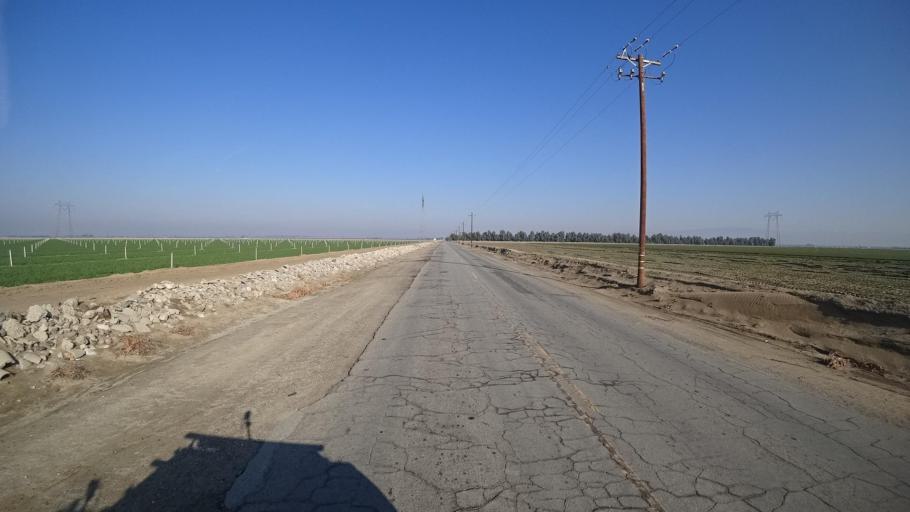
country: US
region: California
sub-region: Kern County
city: Weedpatch
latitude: 35.1228
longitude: -118.9678
